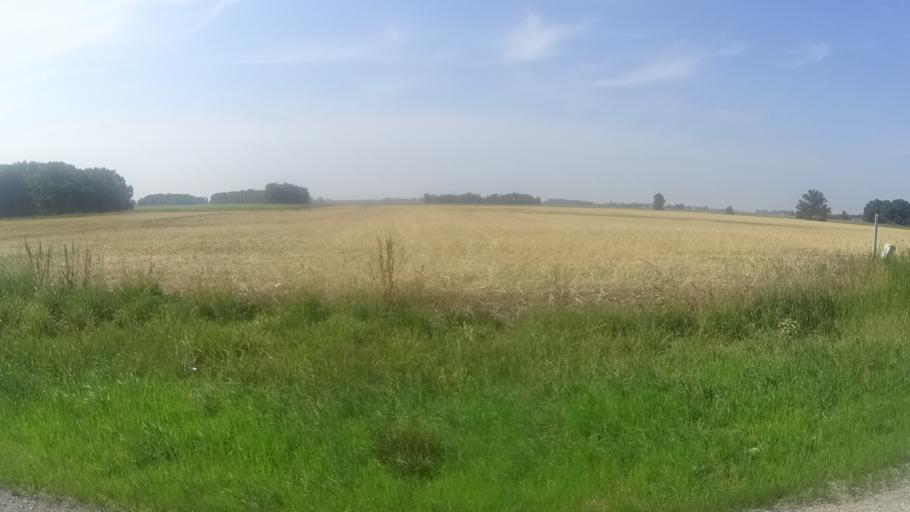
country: US
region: Ohio
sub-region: Huron County
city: Monroeville
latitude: 41.2878
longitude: -82.7400
